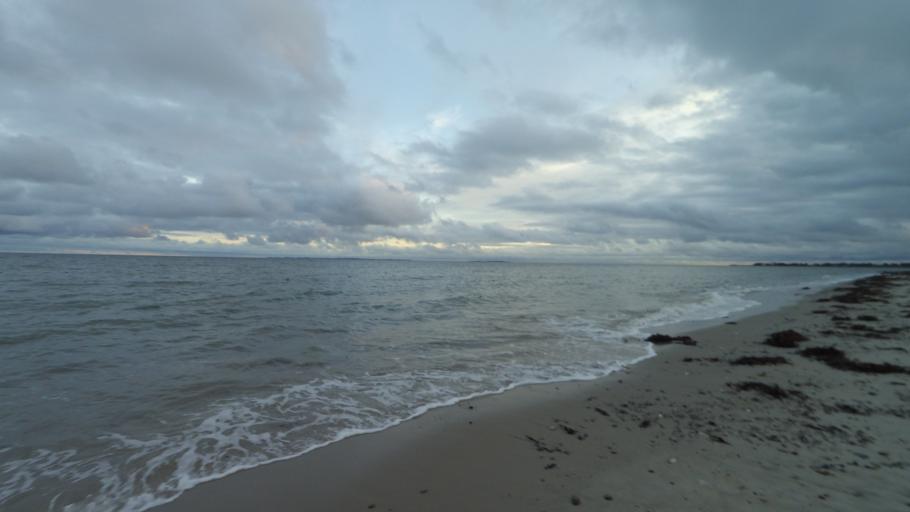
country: DK
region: Central Jutland
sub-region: Arhus Kommune
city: Beder
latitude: 56.0421
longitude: 10.2711
